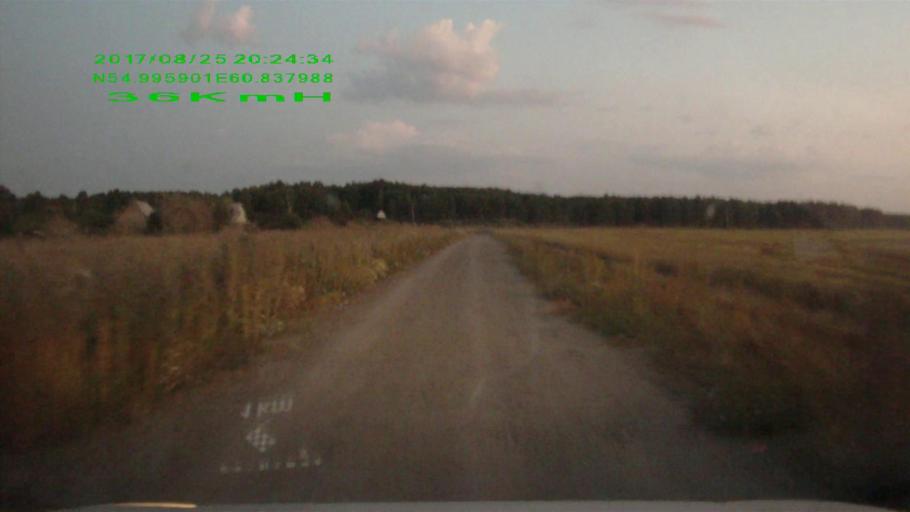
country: RU
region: Chelyabinsk
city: Timiryazevskiy
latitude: 54.9957
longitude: 60.8380
